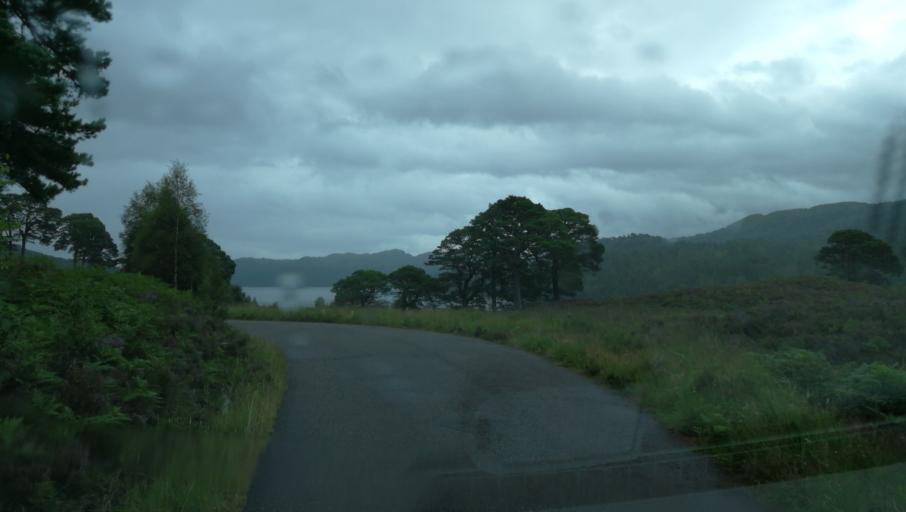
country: GB
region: Scotland
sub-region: Highland
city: Spean Bridge
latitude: 57.2681
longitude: -4.9713
